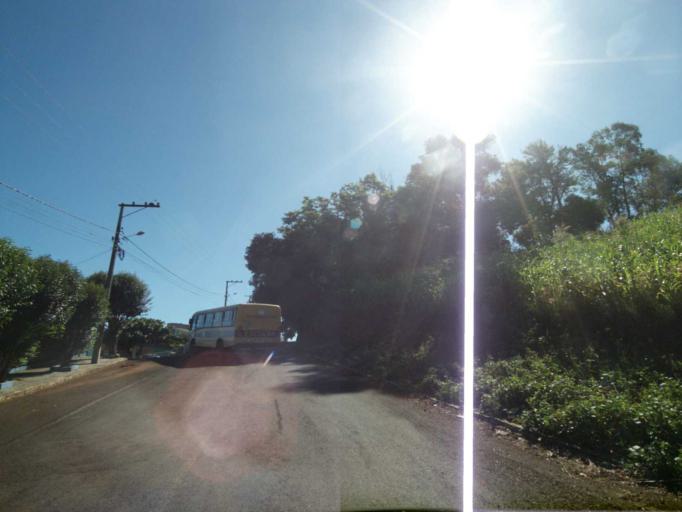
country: BR
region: Parana
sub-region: Coronel Vivida
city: Coronel Vivida
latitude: -25.9600
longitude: -52.8187
